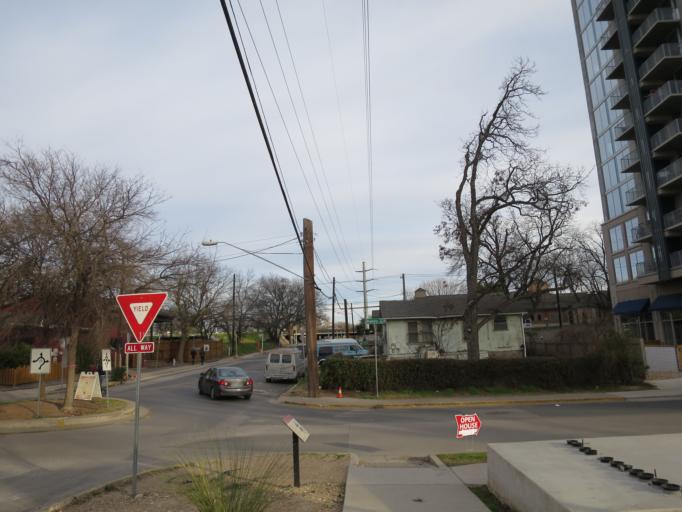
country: US
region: Texas
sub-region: Travis County
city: Austin
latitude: 30.2578
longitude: -97.7393
